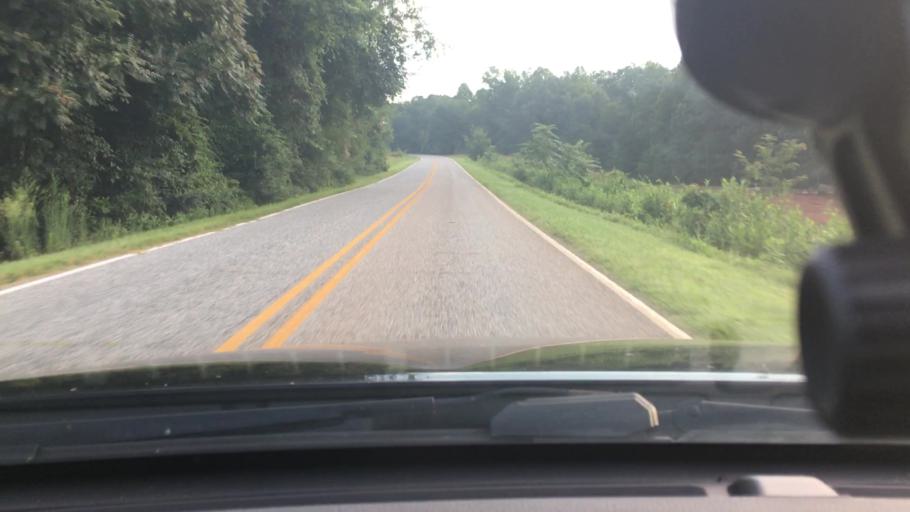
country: US
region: North Carolina
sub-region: Rutherford County
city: Rutherfordton
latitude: 35.3835
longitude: -81.9856
